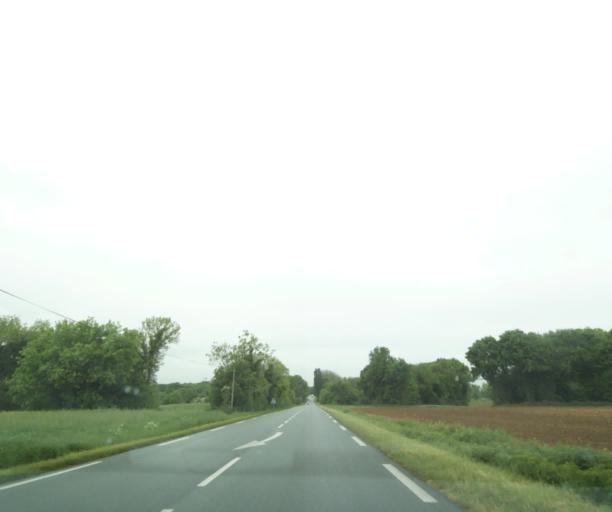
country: FR
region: Poitou-Charentes
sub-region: Departement de la Charente-Maritime
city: Corme-Royal
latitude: 45.7334
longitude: -0.7715
